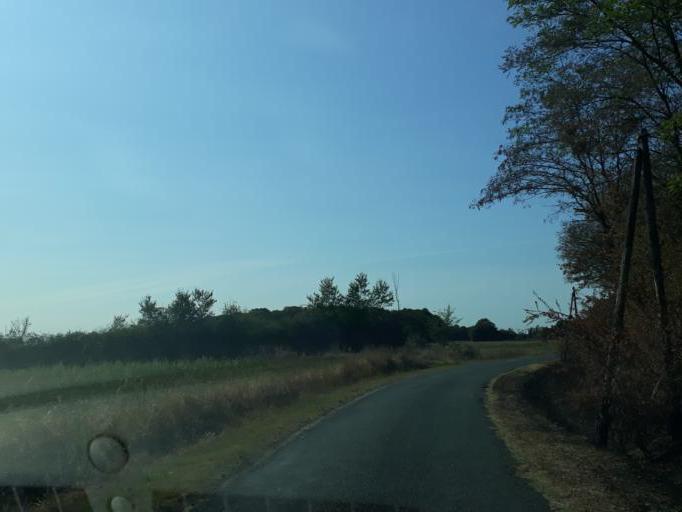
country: FR
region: Centre
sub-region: Departement de l'Indre
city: Chabris
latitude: 47.2611
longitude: 1.6355
